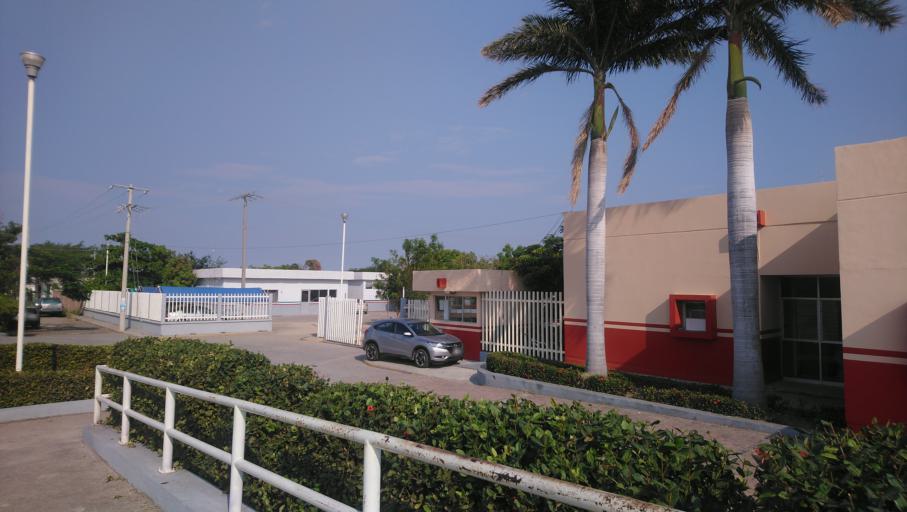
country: MX
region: Oaxaca
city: San Jeronimo Ixtepec
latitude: 16.5589
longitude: -95.1179
